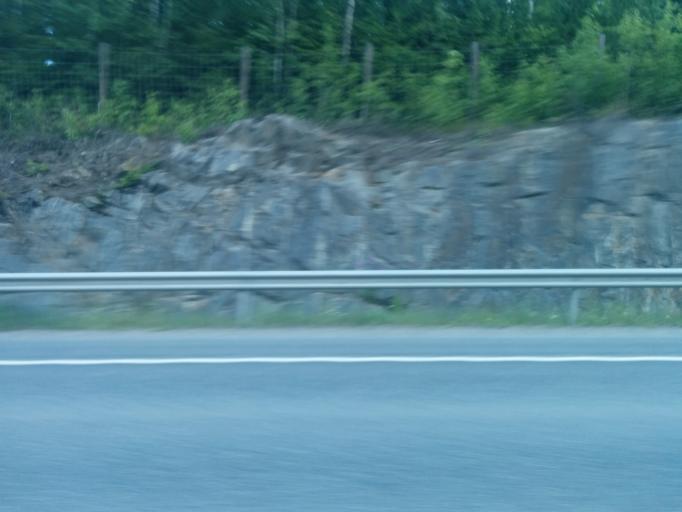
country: FI
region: Pirkanmaa
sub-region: Tampere
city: Kangasala
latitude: 61.5338
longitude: 23.9541
